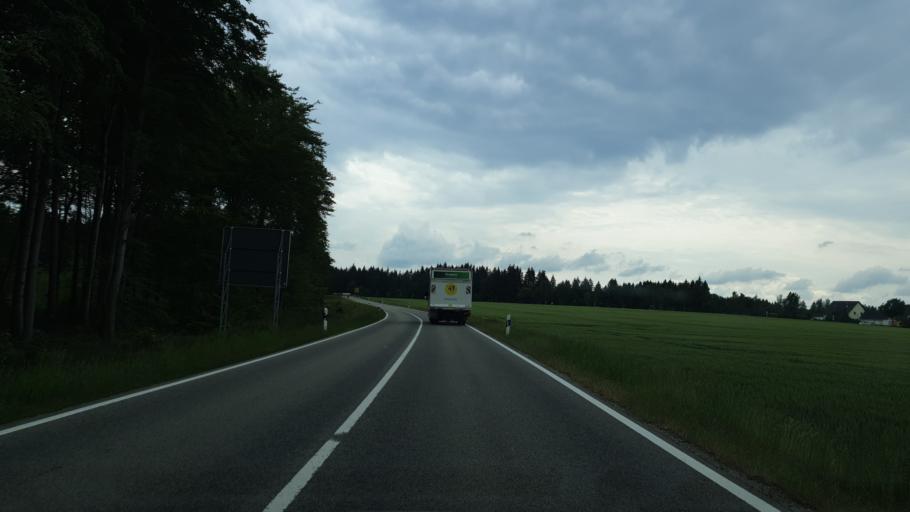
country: DE
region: Saxony
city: Hammerbrucke
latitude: 50.4750
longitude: 12.4323
